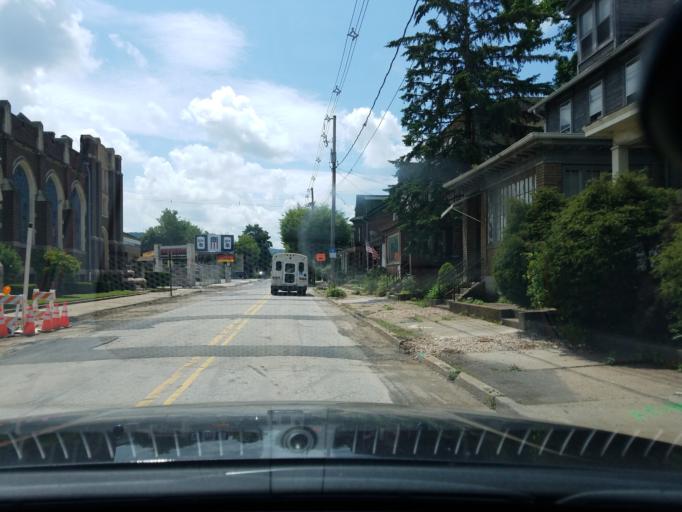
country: US
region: Pennsylvania
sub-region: Cambria County
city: Johnstown
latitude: 40.3199
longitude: -78.9192
